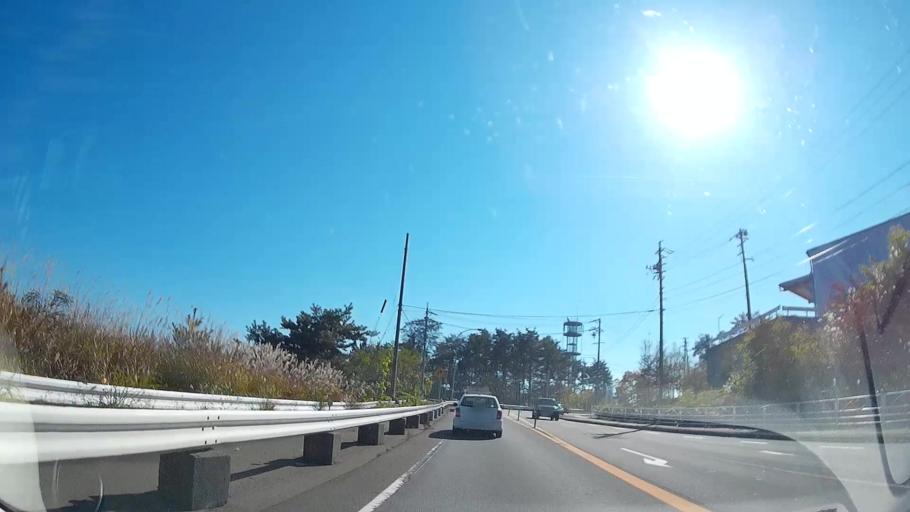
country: JP
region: Nagano
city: Okaya
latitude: 36.0788
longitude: 138.0378
